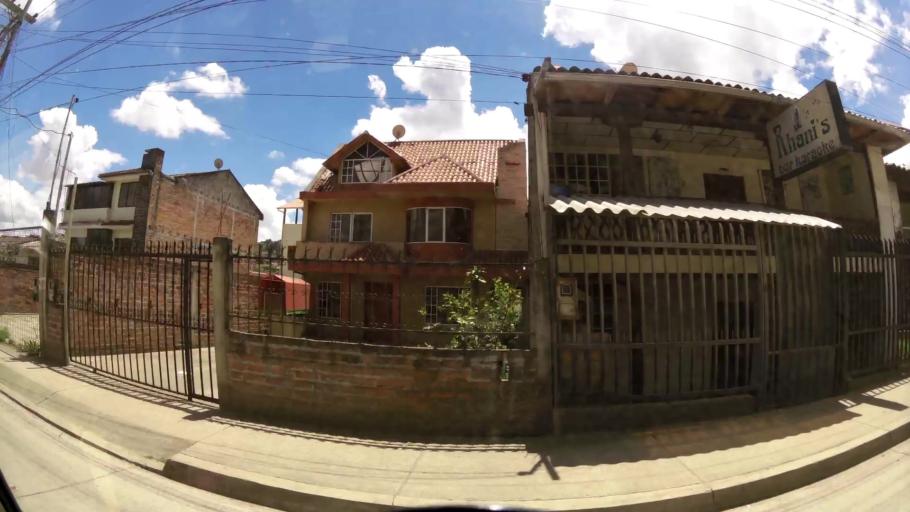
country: EC
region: Azuay
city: Cuenca
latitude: -2.9323
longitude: -79.0439
